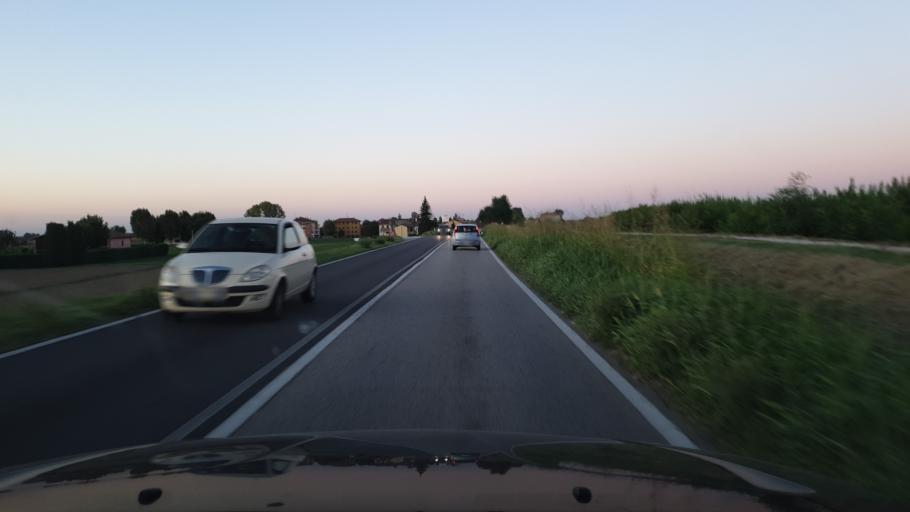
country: IT
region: Emilia-Romagna
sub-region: Provincia di Bologna
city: Ca De Fabbri
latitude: 44.6238
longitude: 11.4573
